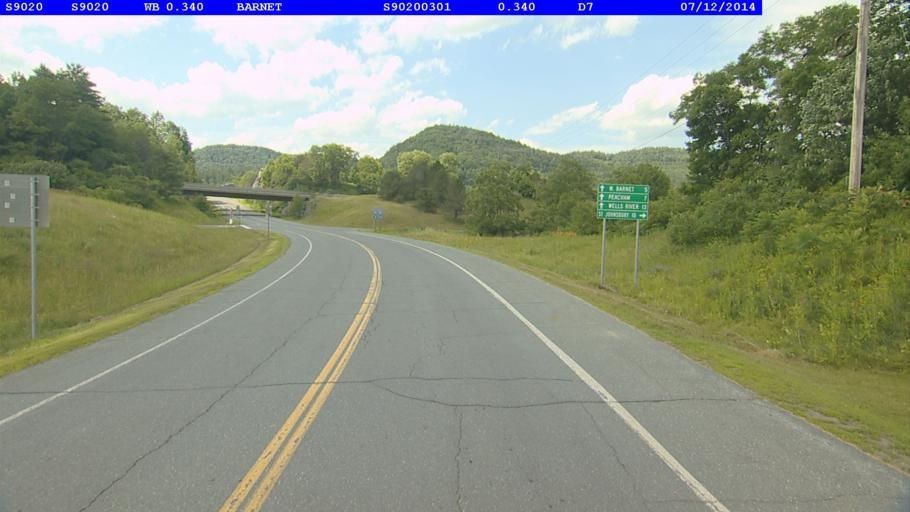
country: US
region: Vermont
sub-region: Caledonia County
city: Saint Johnsbury
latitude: 44.2972
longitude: -72.0554
